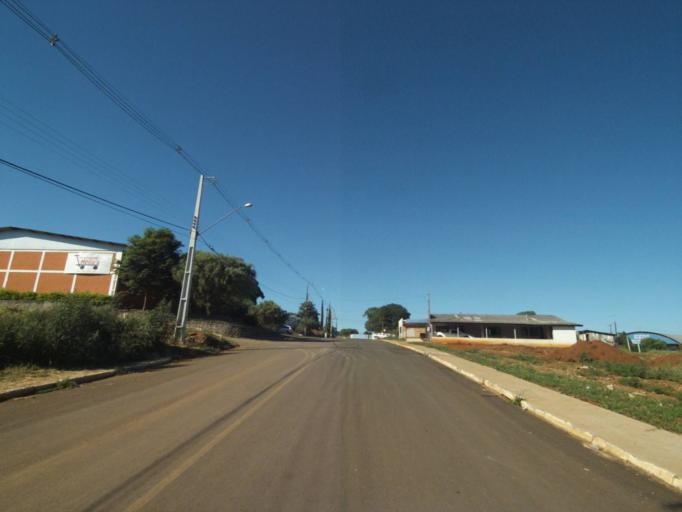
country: BR
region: Parana
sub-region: Pinhao
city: Pinhao
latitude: -25.8408
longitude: -52.0289
